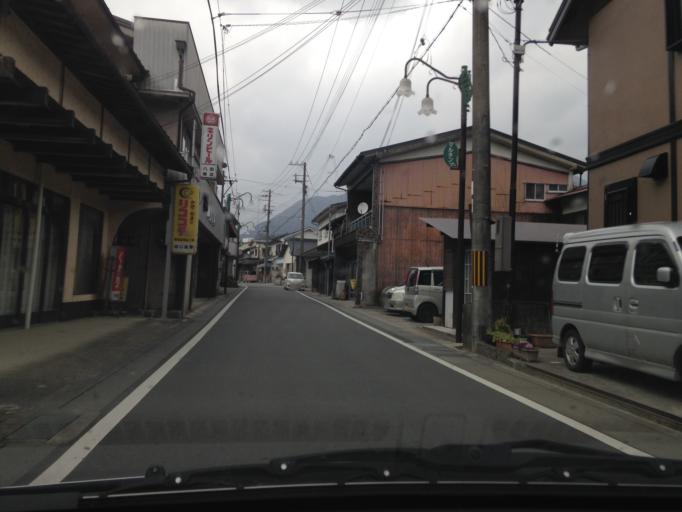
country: JP
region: Hyogo
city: Yamazakicho-nakabirose
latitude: 35.1499
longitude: 134.4444
